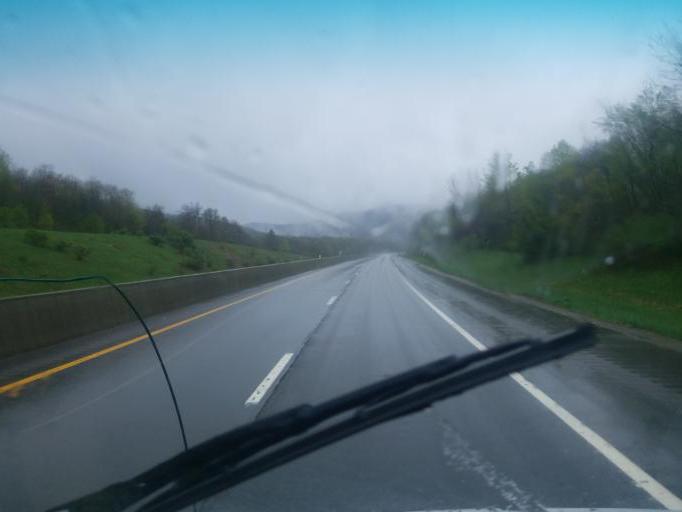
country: US
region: New York
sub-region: Cattaraugus County
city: Salamanca
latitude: 42.0948
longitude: -78.6543
